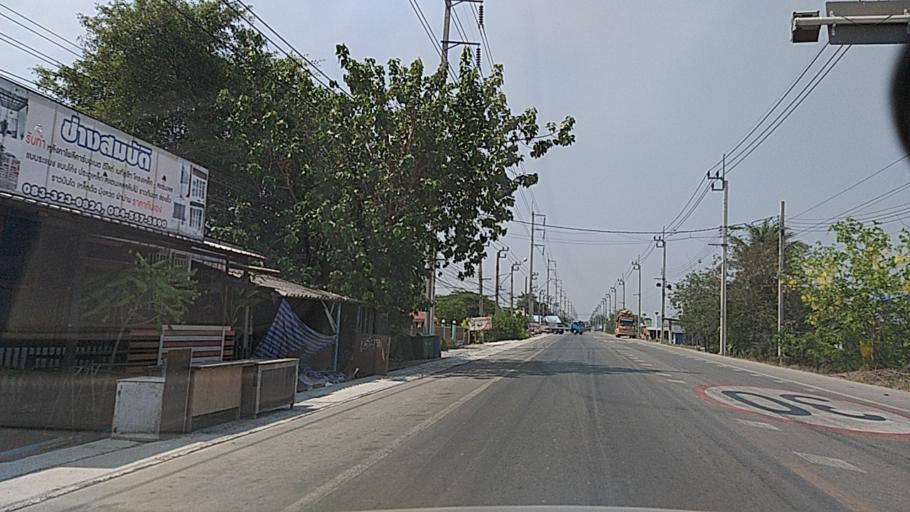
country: TH
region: Nonthaburi
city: Sai Noi
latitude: 13.9216
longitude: 100.3206
